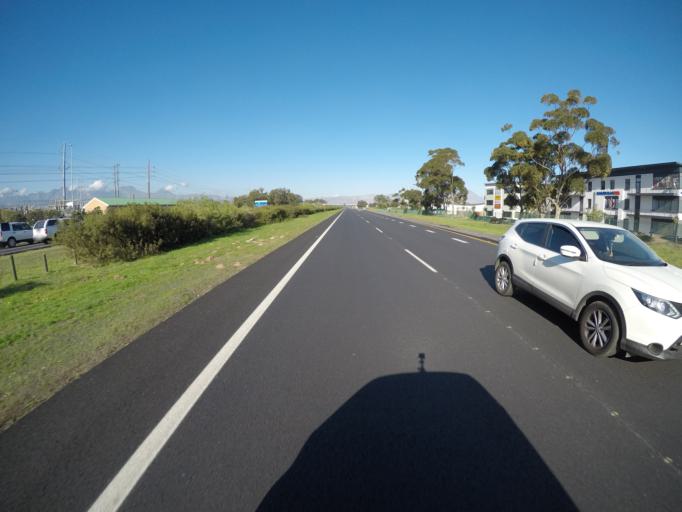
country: ZA
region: Western Cape
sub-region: Cape Winelands District Municipality
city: Stellenbosch
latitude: -34.0733
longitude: 18.8166
